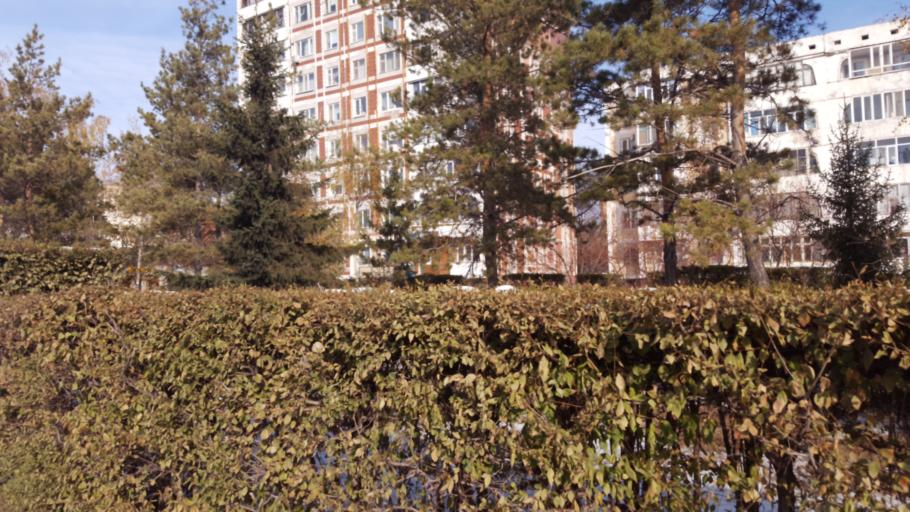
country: KZ
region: Astana Qalasy
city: Astana
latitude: 51.1561
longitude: 71.4825
